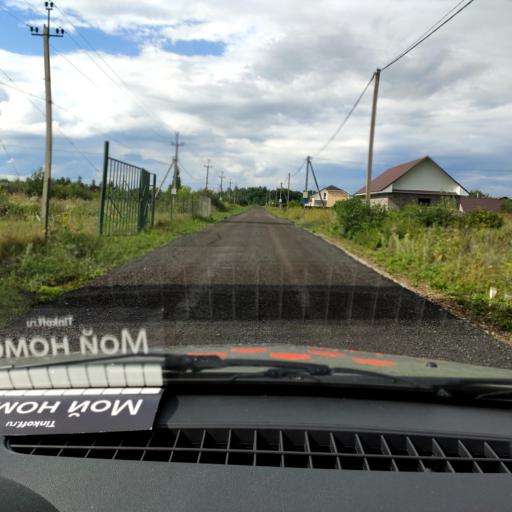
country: RU
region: Bashkortostan
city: Avdon
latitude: 54.5199
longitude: 55.8336
